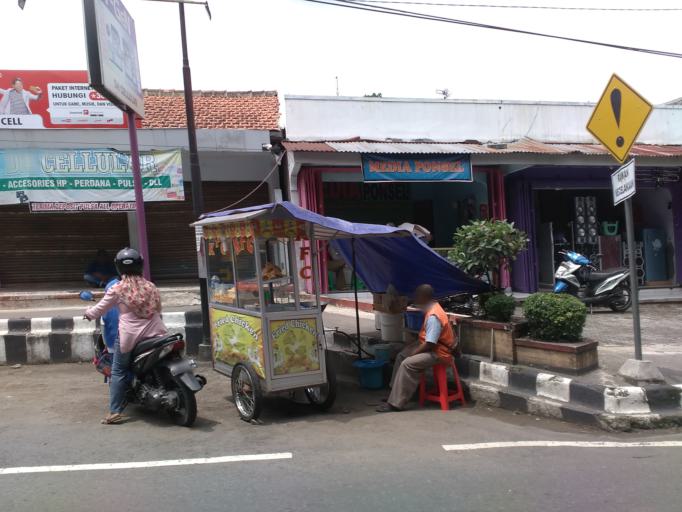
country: ID
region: Central Java
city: Boyolali
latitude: -7.5435
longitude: 110.6023
